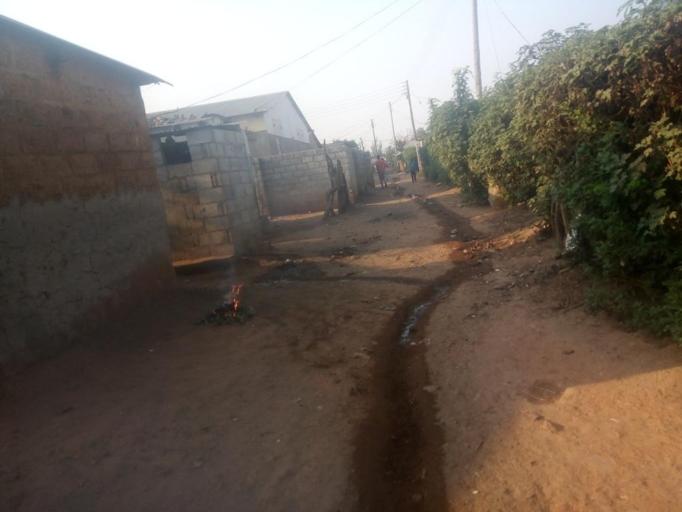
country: ZM
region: Lusaka
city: Lusaka
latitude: -15.4071
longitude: 28.3659
